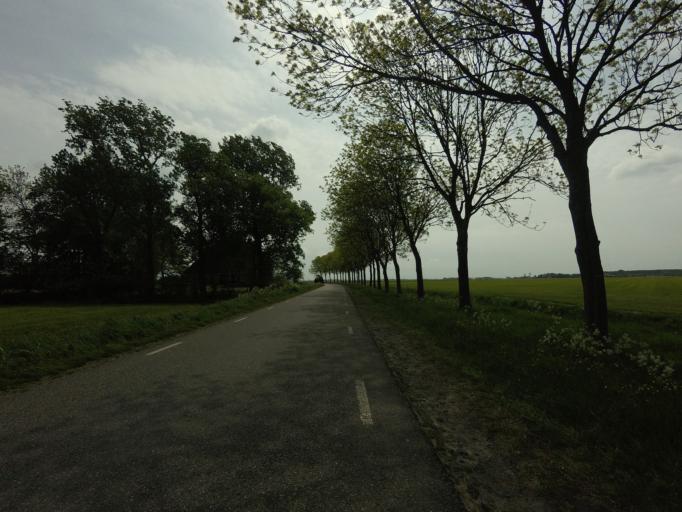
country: NL
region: Friesland
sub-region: Sudwest Fryslan
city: Bolsward
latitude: 53.1100
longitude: 5.4915
